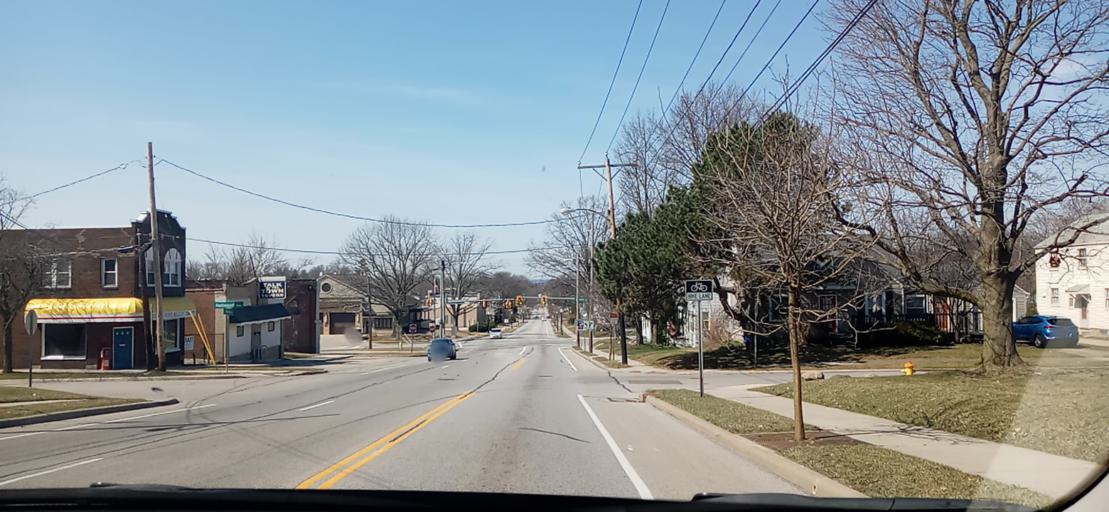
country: US
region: Ohio
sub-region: Summit County
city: Portage Lakes
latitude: 41.0399
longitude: -81.5089
